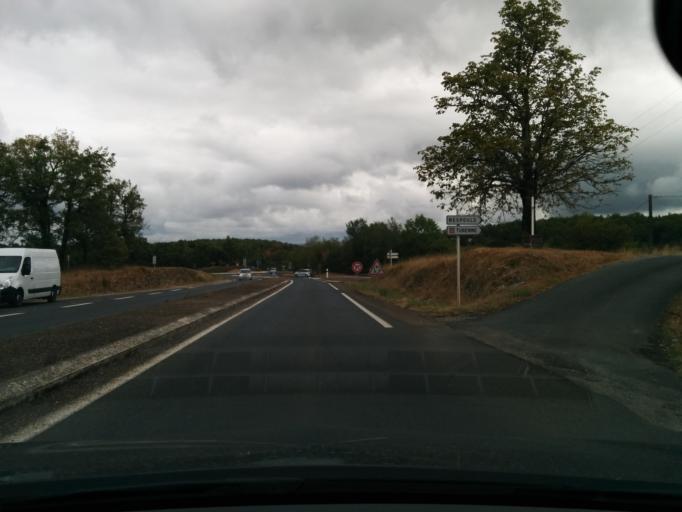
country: FR
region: Limousin
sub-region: Departement de la Correze
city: Saint-Pantaleon-de-Larche
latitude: 45.0508
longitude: 1.4971
